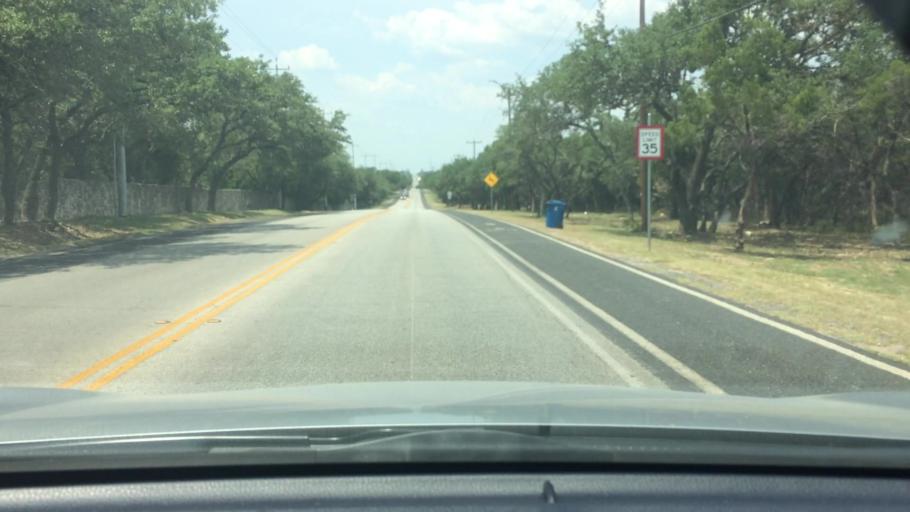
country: US
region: Texas
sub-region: Bexar County
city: Shavano Park
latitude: 29.5839
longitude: -98.5546
